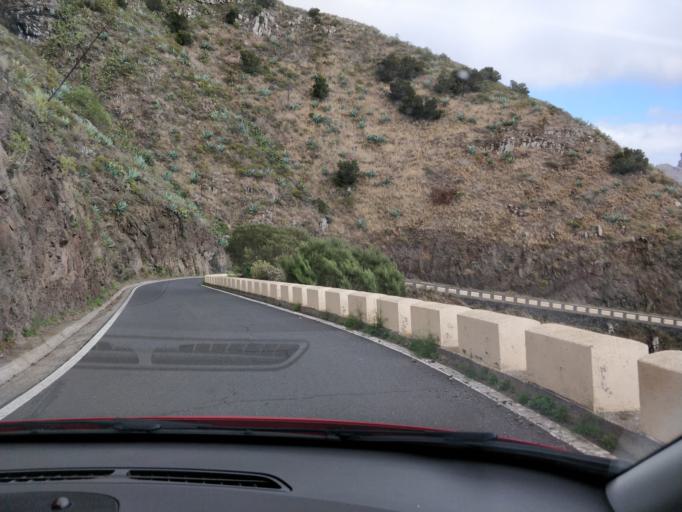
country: ES
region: Canary Islands
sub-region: Provincia de Santa Cruz de Tenerife
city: Tanque
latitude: 28.3244
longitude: -16.8570
